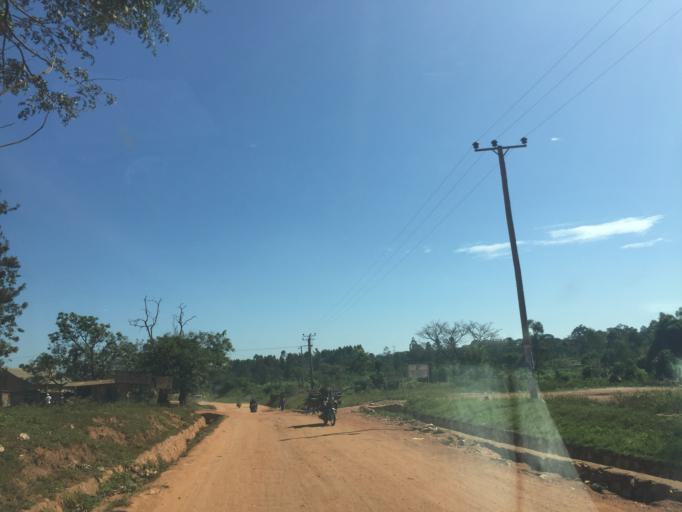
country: UG
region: Central Region
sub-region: Luwero District
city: Luwero
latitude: 0.8366
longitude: 32.5030
